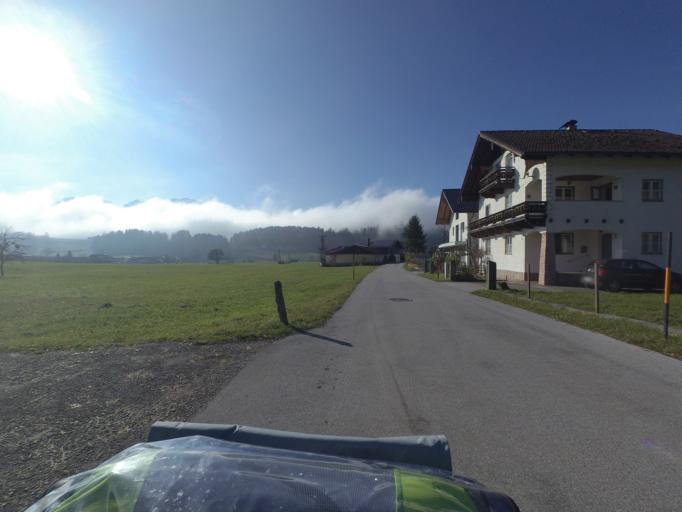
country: AT
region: Salzburg
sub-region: Politischer Bezirk Hallein
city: Adnet
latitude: 47.6871
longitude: 13.1443
